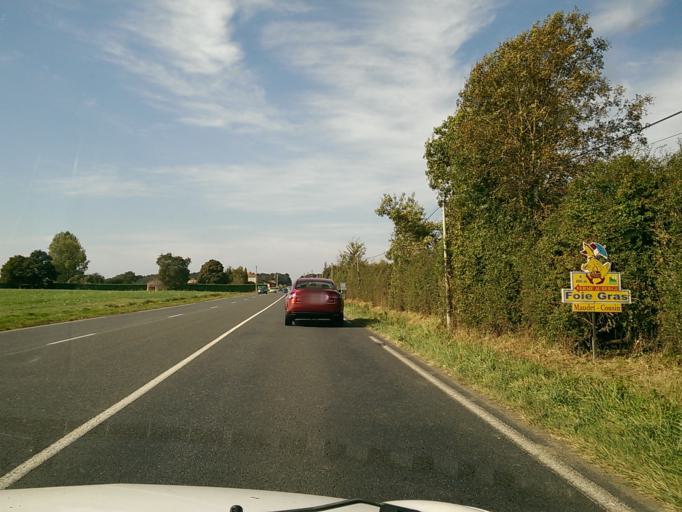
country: FR
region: Pays de la Loire
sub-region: Departement de Maine-et-Loire
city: Vihiers
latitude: 47.1506
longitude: -0.4706
